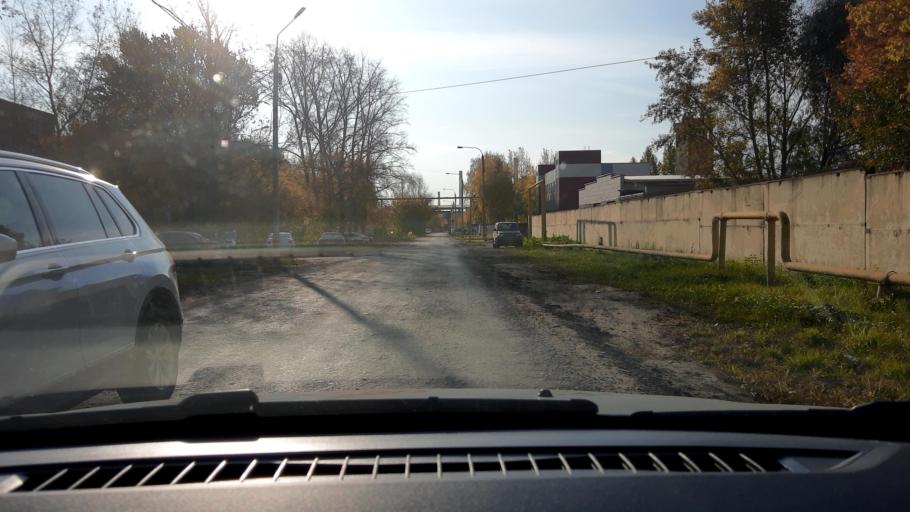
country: RU
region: Nizjnij Novgorod
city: Gorbatovka
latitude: 56.2566
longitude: 43.8773
